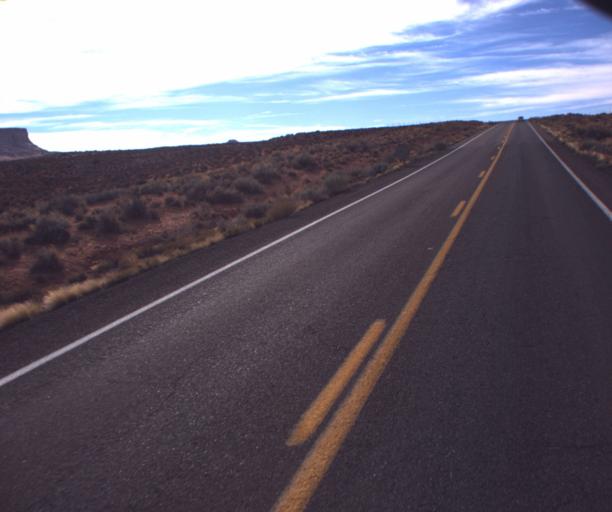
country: US
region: Arizona
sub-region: Coconino County
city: LeChee
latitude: 36.8715
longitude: -111.3419
